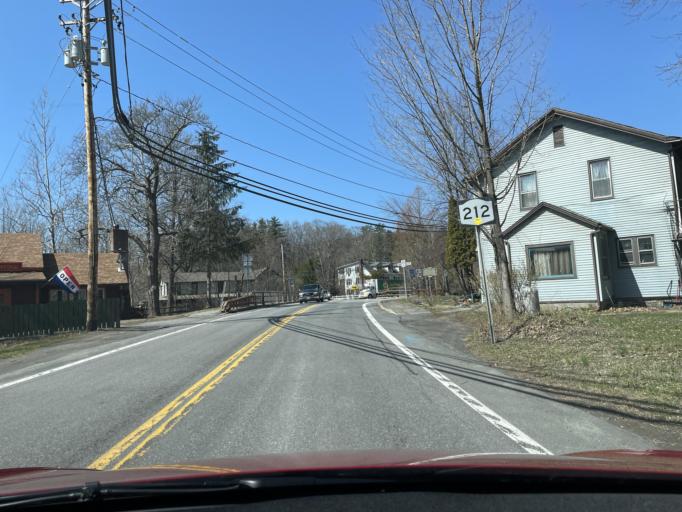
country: US
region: New York
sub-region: Ulster County
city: Woodstock
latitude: 42.0406
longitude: -74.1541
